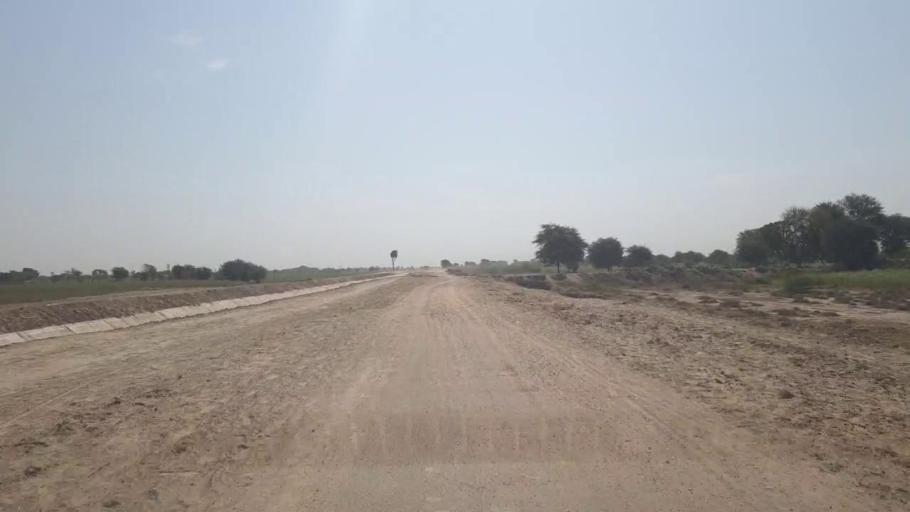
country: PK
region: Sindh
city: Kunri
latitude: 25.2709
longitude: 69.6259
